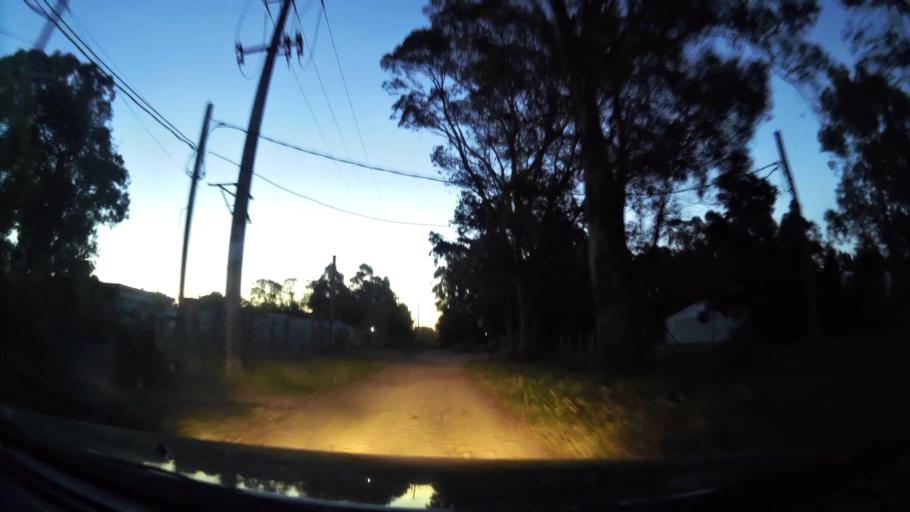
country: UY
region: Canelones
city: Atlantida
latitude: -34.7626
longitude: -55.7582
